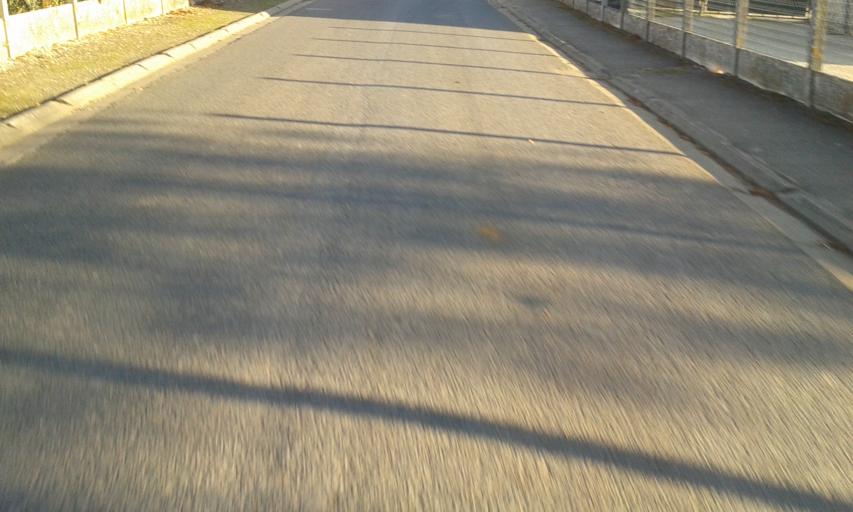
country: FR
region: Centre
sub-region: Departement du Loir-et-Cher
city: Ouzouer-le-Marche
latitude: 47.8797
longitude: 1.4194
